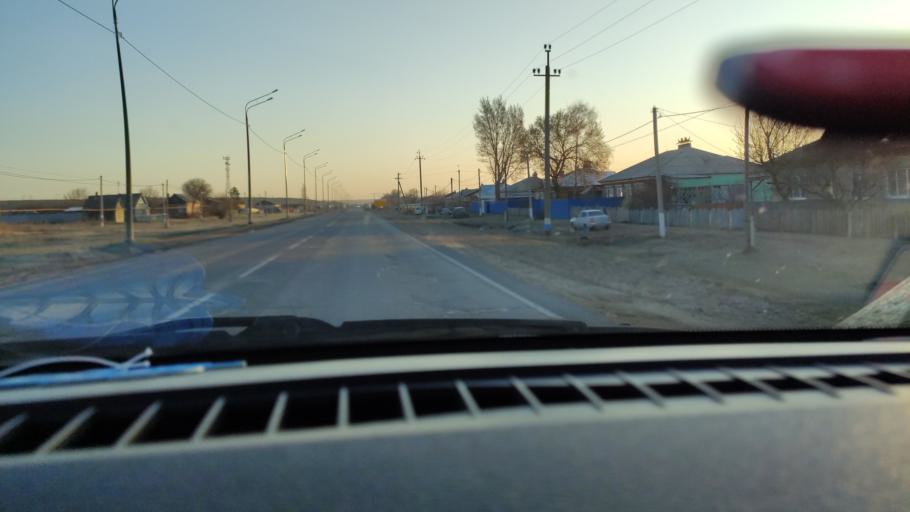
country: RU
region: Saratov
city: Sinodskoye
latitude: 51.9930
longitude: 46.6706
